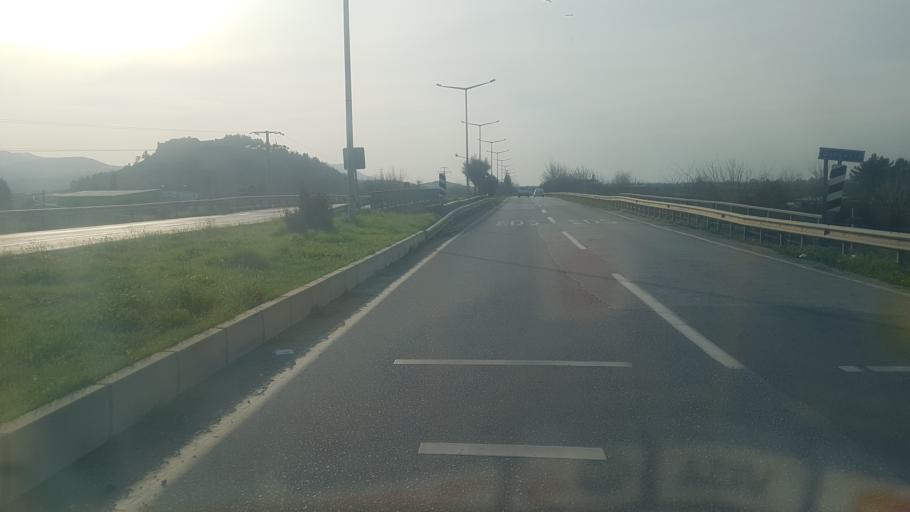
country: TR
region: Osmaniye
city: Toprakkale
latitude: 37.0527
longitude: 36.1489
